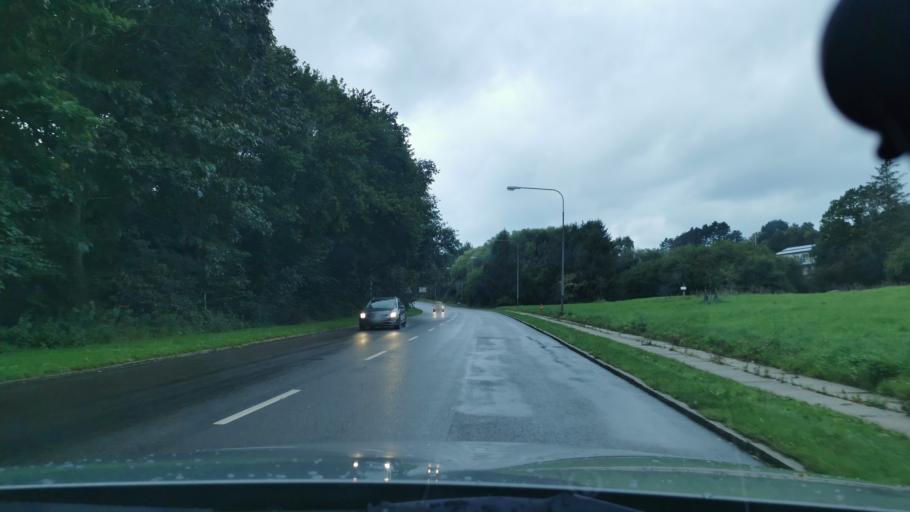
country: DK
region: Zealand
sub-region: Kalundborg Kommune
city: Kalundborg
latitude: 55.6873
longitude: 11.0717
